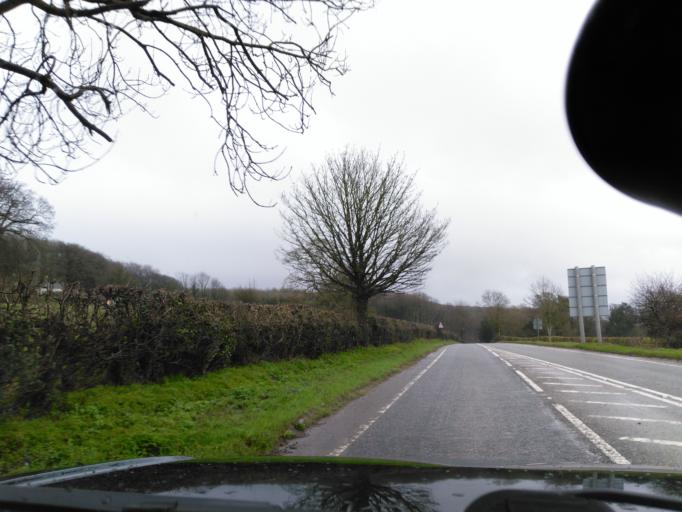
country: GB
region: England
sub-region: Somerset
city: Evercreech
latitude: 51.1957
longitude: -2.4586
